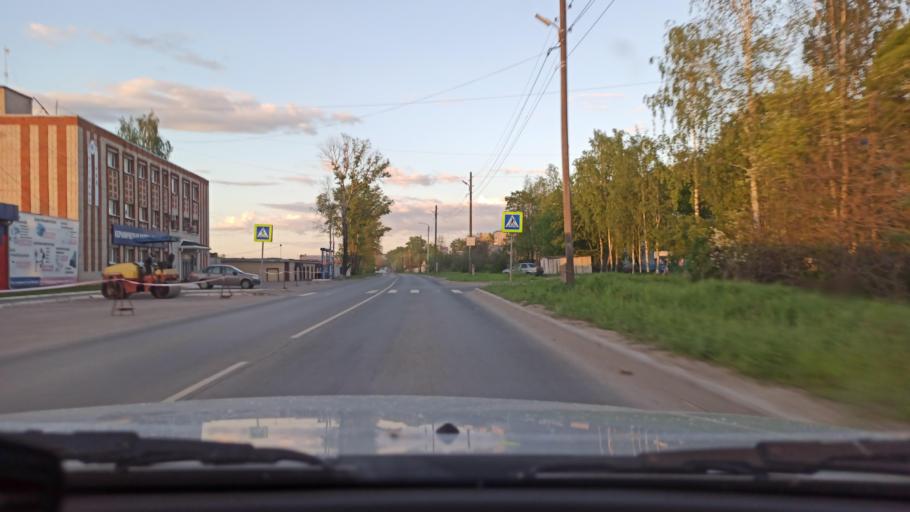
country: RU
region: Vologda
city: Vologda
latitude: 59.2203
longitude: 39.8338
